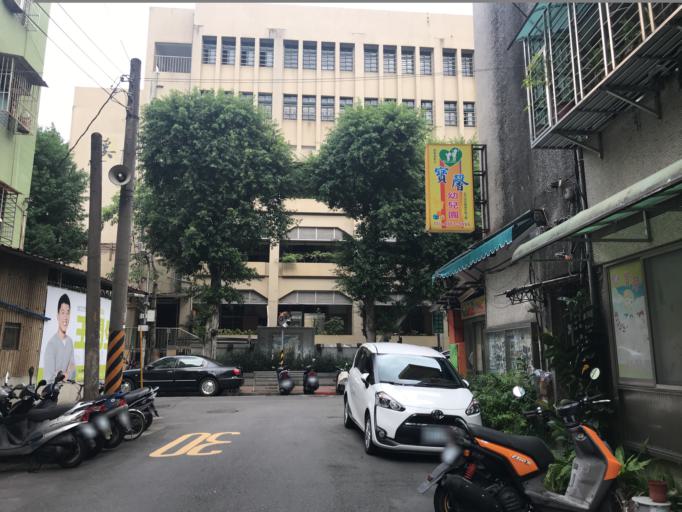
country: TW
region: Taipei
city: Taipei
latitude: 24.9950
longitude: 121.5384
